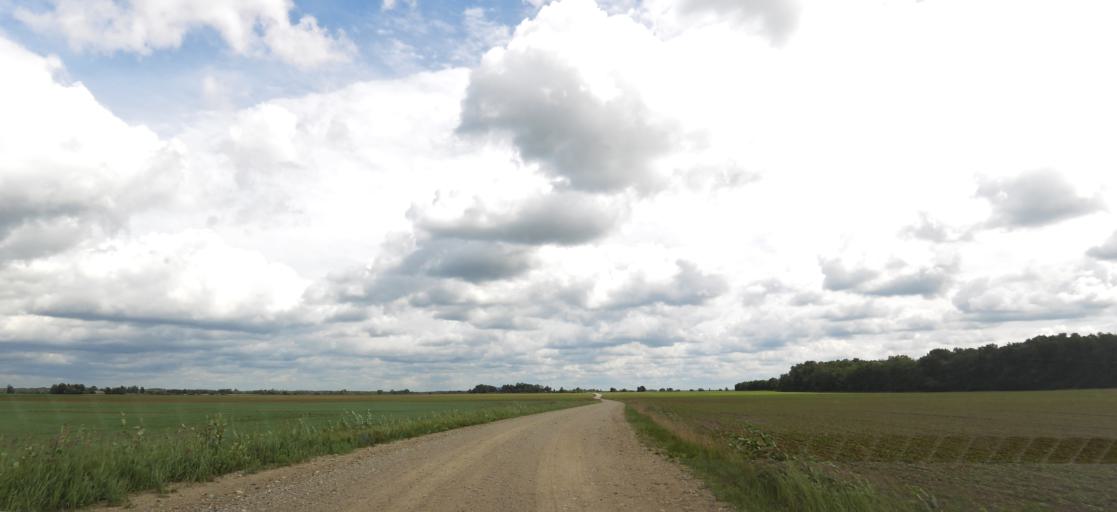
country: LT
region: Panevezys
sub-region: Birzai
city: Birzai
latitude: 56.3151
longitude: 24.7473
